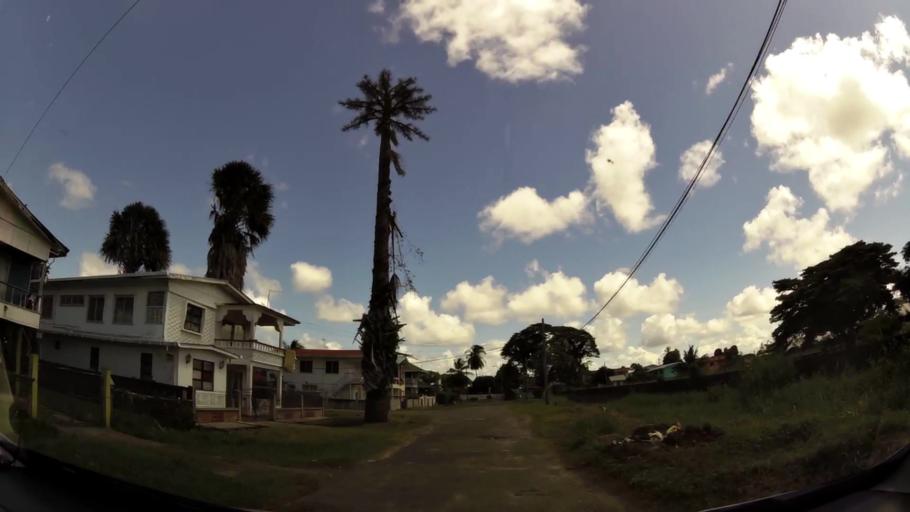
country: GY
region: Demerara-Mahaica
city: Georgetown
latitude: 6.7976
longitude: -58.1358
